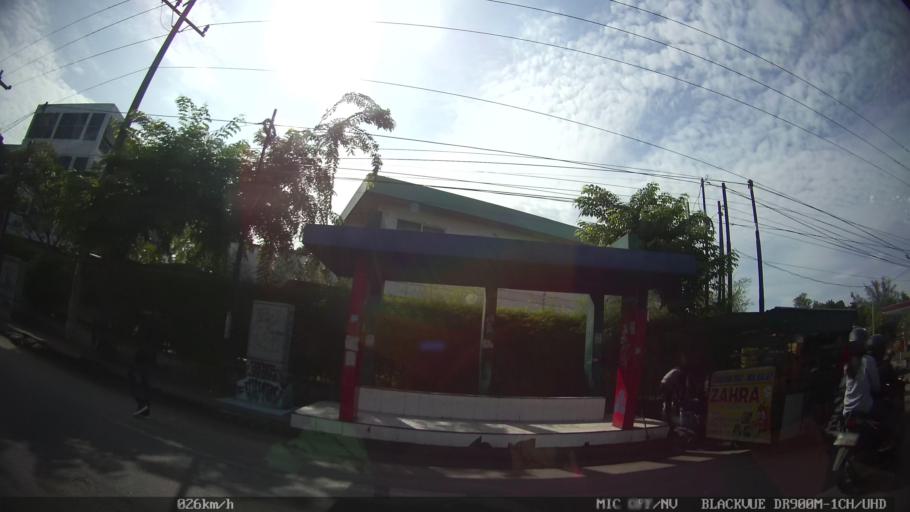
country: ID
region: North Sumatra
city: Medan
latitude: 3.5900
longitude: 98.6435
